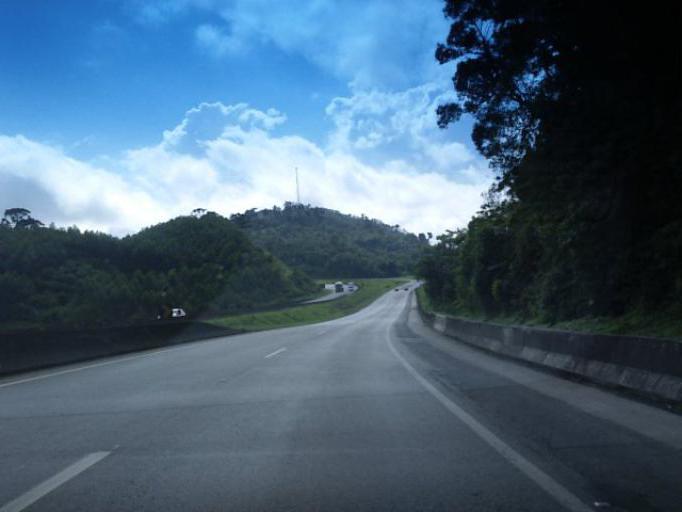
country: BR
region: Parana
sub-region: Antonina
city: Antonina
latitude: -25.1112
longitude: -48.7512
